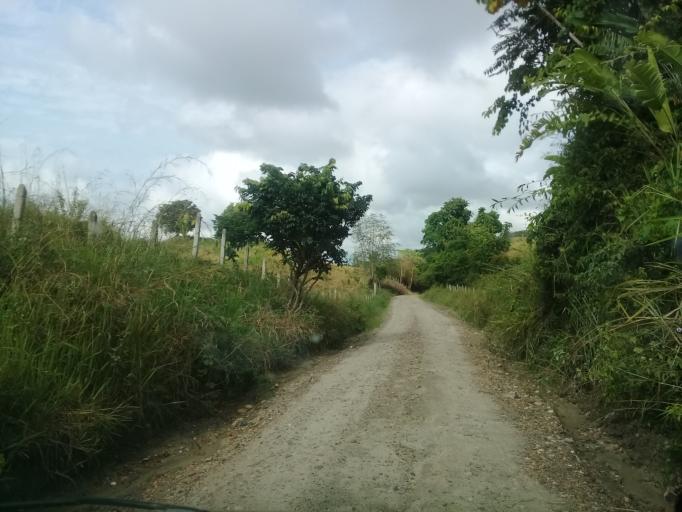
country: CO
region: Antioquia
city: Puerto Triunfo
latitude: 5.7101
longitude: -74.5764
